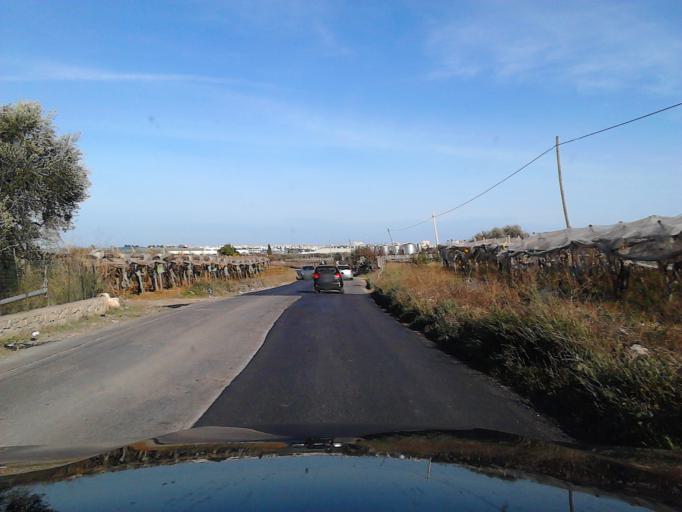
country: IT
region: Apulia
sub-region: Provincia di Bari
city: Noicattaro
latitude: 41.0177
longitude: 16.9663
